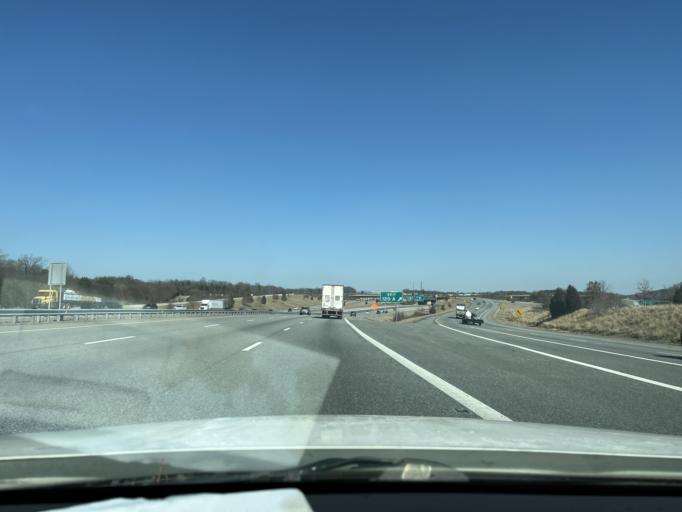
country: US
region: North Carolina
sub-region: Guilford County
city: Jamestown
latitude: 35.9998
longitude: -79.8605
